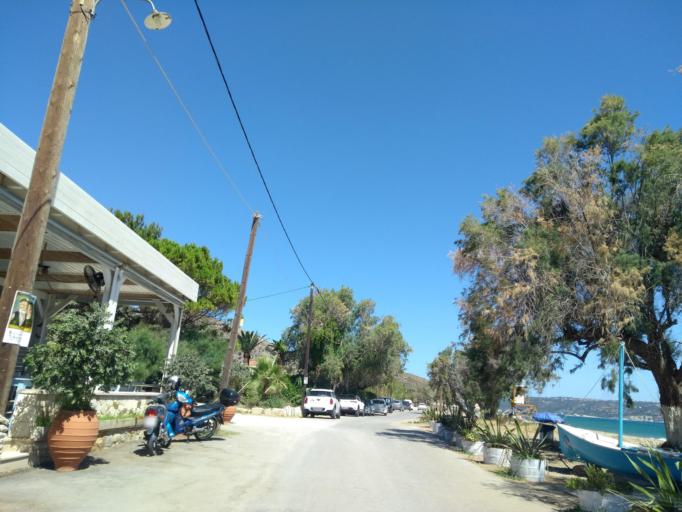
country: GR
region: Crete
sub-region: Nomos Chanias
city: Kalivai
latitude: 35.4608
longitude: 24.1613
